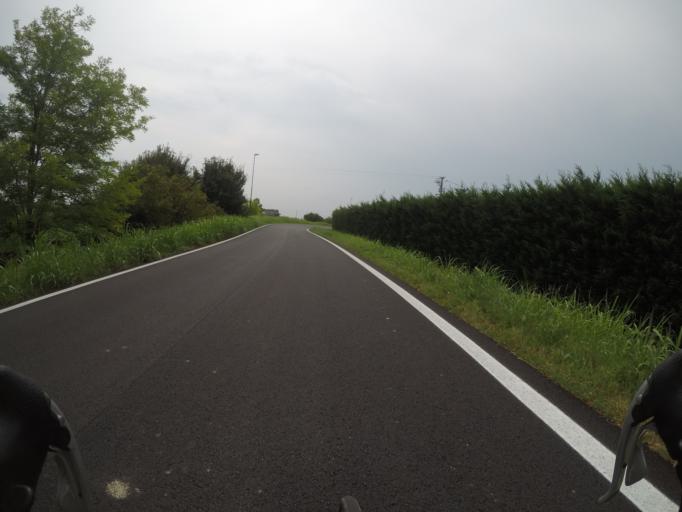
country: IT
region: Veneto
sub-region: Provincia di Rovigo
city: Costa di Rovigo
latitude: 45.0486
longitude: 11.6750
